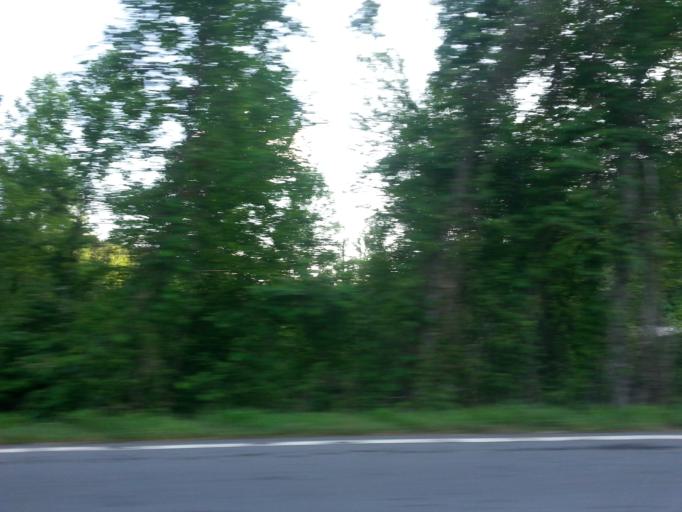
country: US
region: North Carolina
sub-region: Cherokee County
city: Murphy
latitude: 35.0921
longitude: -84.2111
